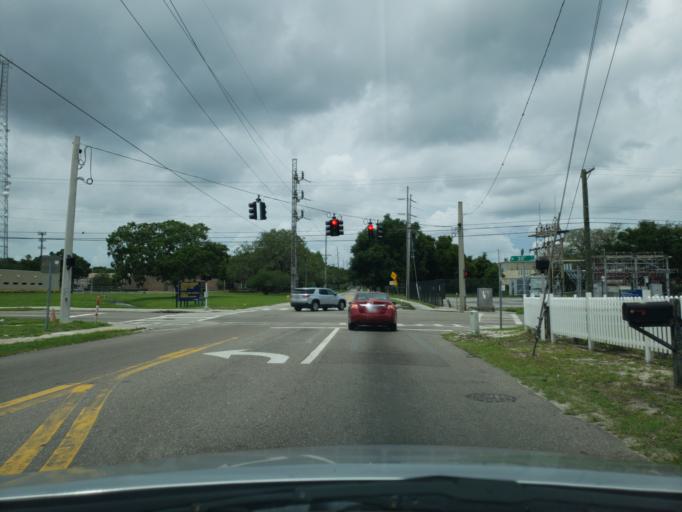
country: US
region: Florida
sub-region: Hillsborough County
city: Temple Terrace
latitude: 28.0034
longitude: -82.4262
